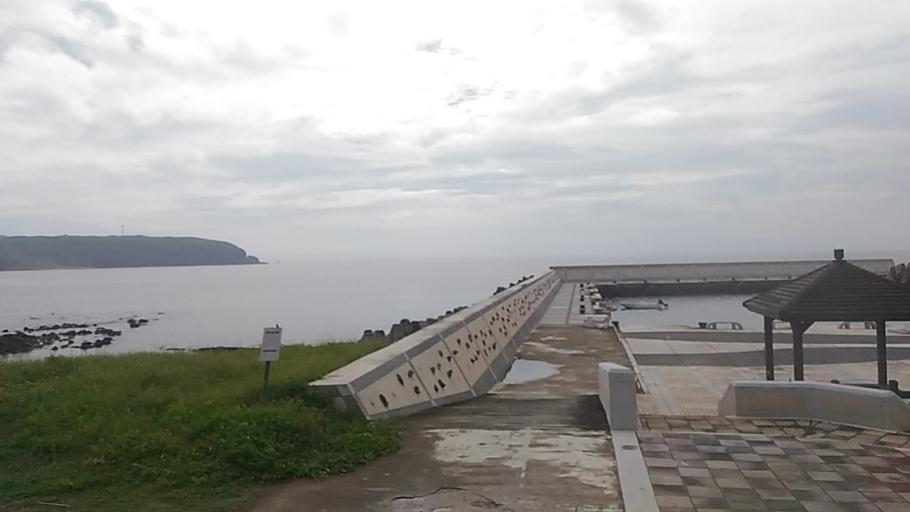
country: TW
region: Taiwan
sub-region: Penghu
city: Ma-kung
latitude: 23.1941
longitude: 119.4289
